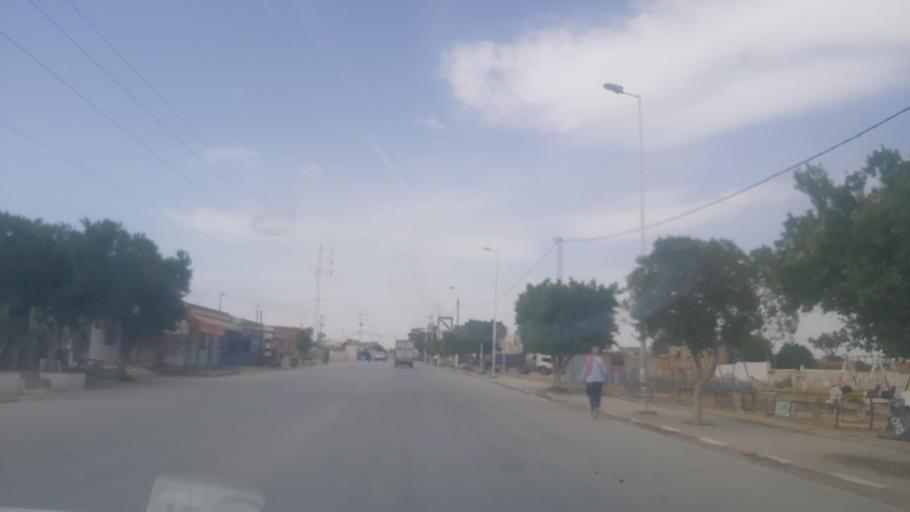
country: TN
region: Silyanah
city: Bu `Aradah
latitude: 36.3511
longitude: 9.6268
